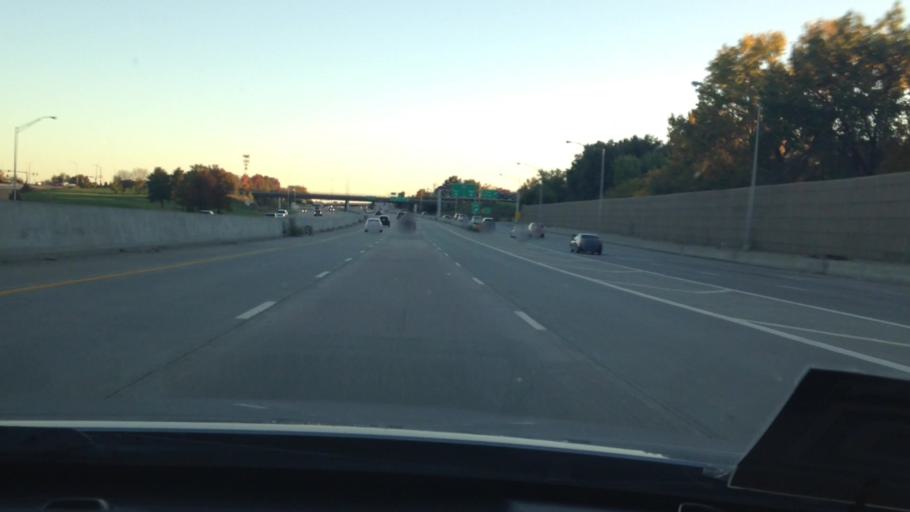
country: US
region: Kansas
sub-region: Johnson County
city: Lenexa
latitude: 38.9467
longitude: -94.7056
